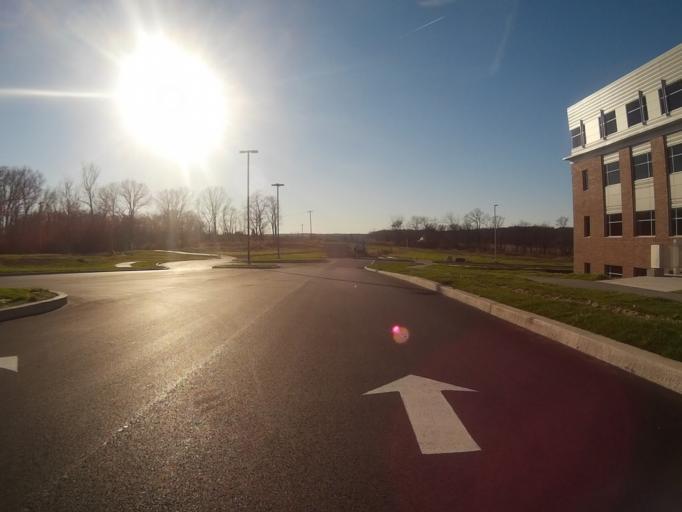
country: US
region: Pennsylvania
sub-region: Centre County
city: Houserville
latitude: 40.8287
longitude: -77.8487
